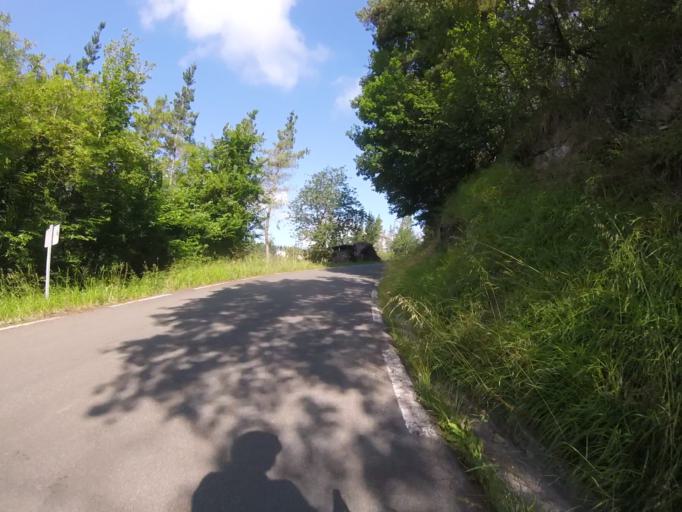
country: ES
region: Basque Country
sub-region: Provincia de Guipuzcoa
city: Beasain
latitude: 43.0775
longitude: -2.2233
